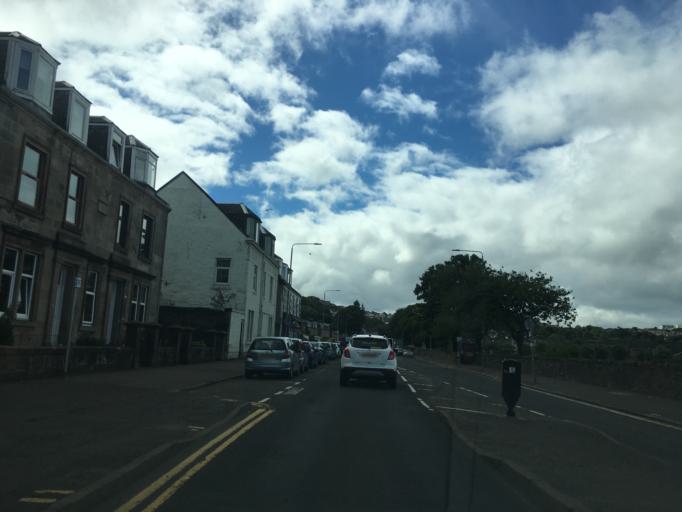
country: GB
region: Scotland
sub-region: Inverclyde
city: Gourock
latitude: 55.9584
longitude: -4.7991
